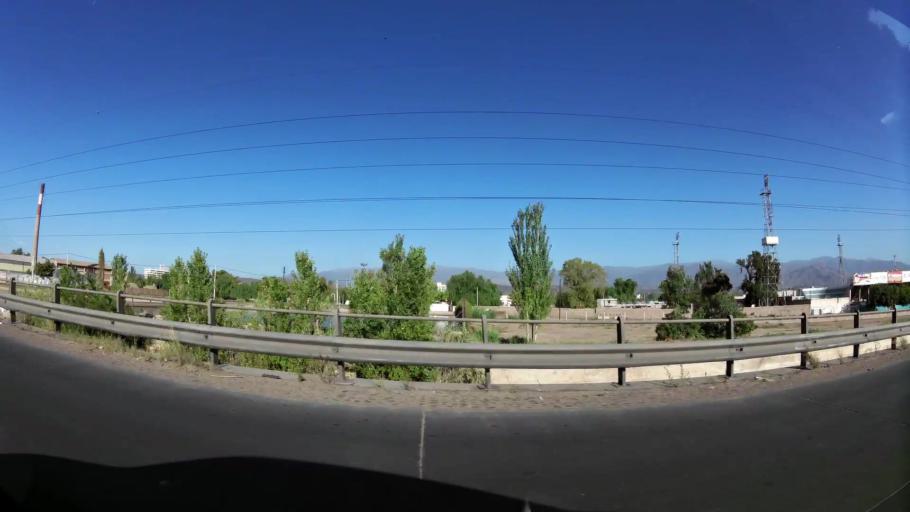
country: AR
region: Mendoza
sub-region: Departamento de Godoy Cruz
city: Godoy Cruz
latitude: -32.9216
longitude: -68.8376
